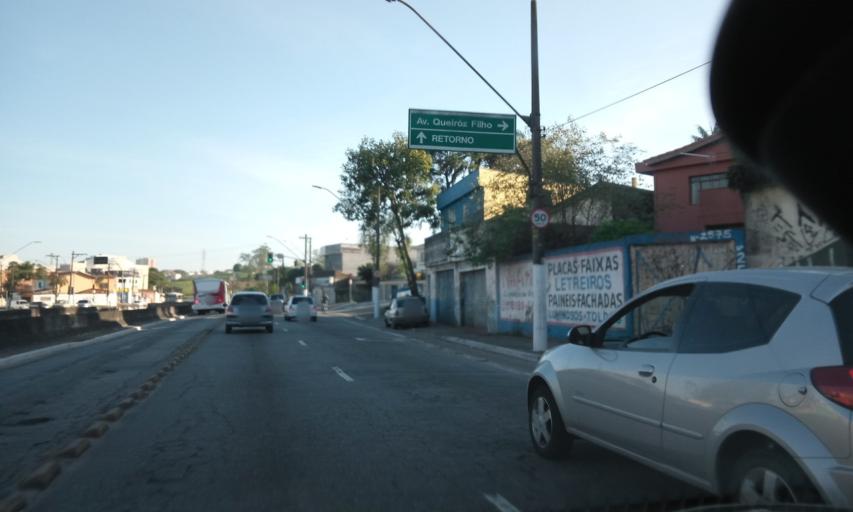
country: BR
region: Sao Paulo
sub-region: Santo Andre
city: Santo Andre
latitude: -23.6854
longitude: -46.5063
